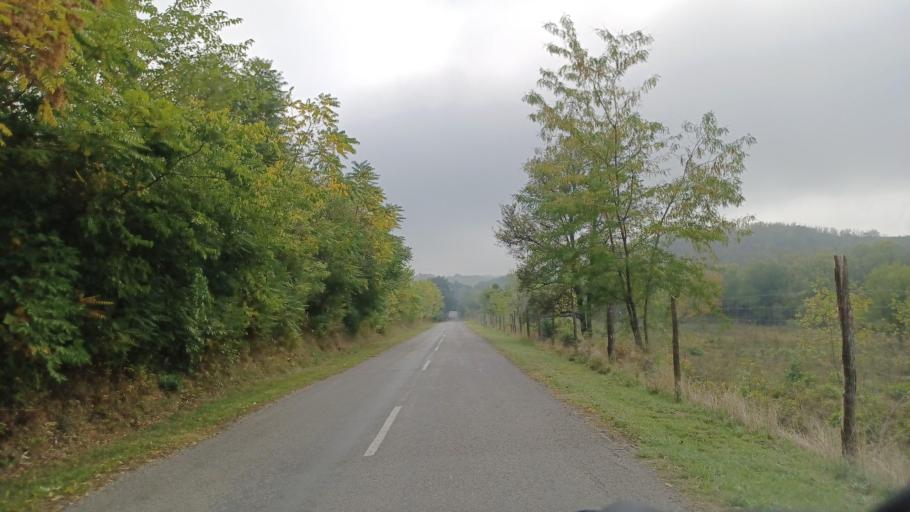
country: HU
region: Tolna
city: Pincehely
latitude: 46.6546
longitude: 18.5053
